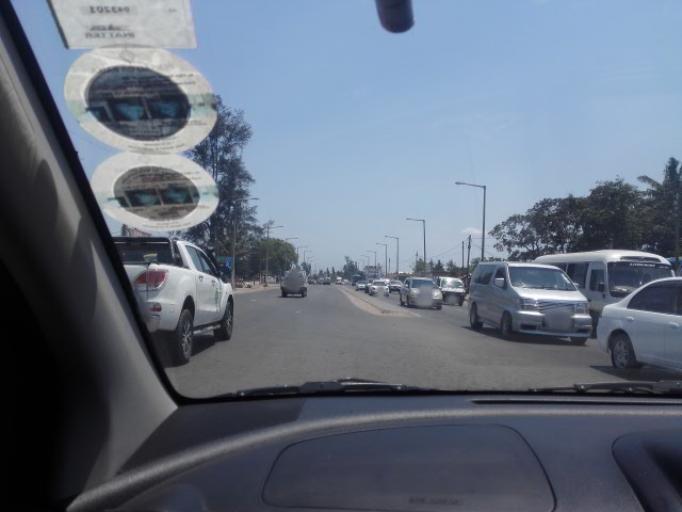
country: MZ
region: Maputo City
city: Maputo
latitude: -25.8983
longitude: 32.5639
